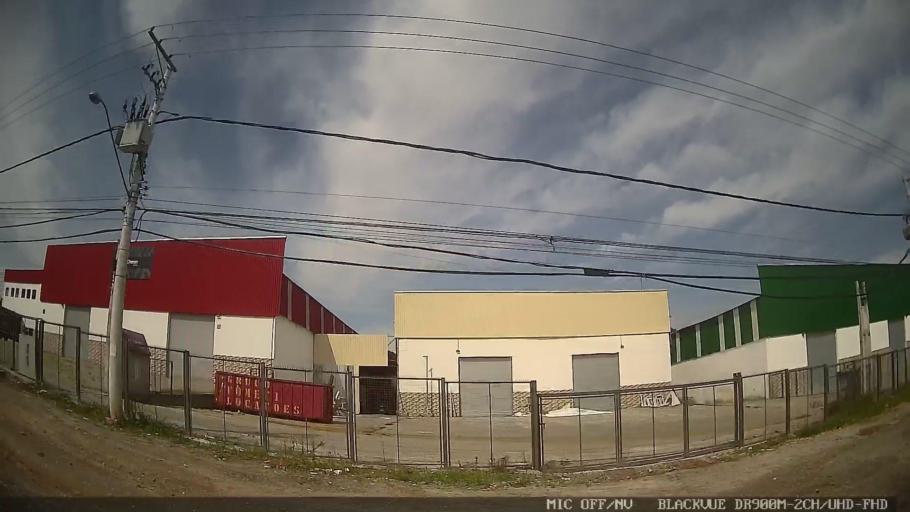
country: BR
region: Sao Paulo
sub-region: Itaquaquecetuba
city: Itaquaquecetuba
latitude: -23.4771
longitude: -46.2948
